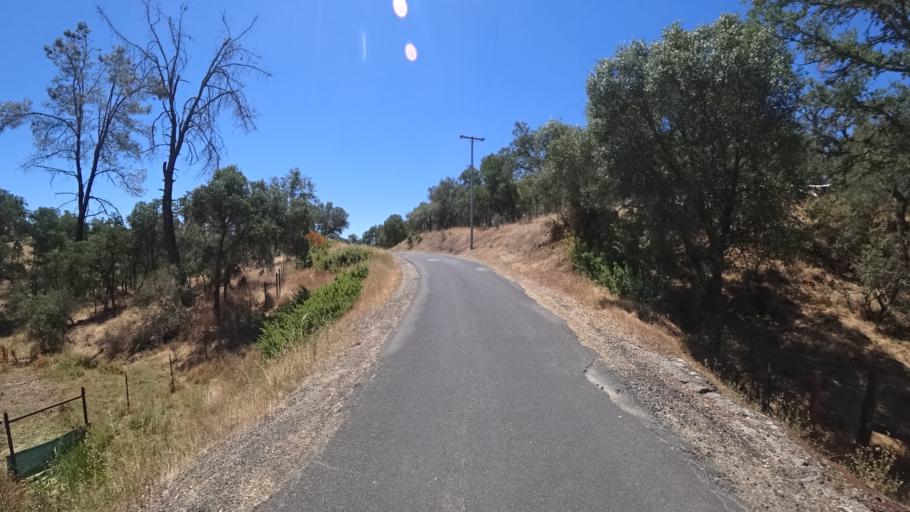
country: US
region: California
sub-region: Calaveras County
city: Copperopolis
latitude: 37.9859
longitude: -120.7024
